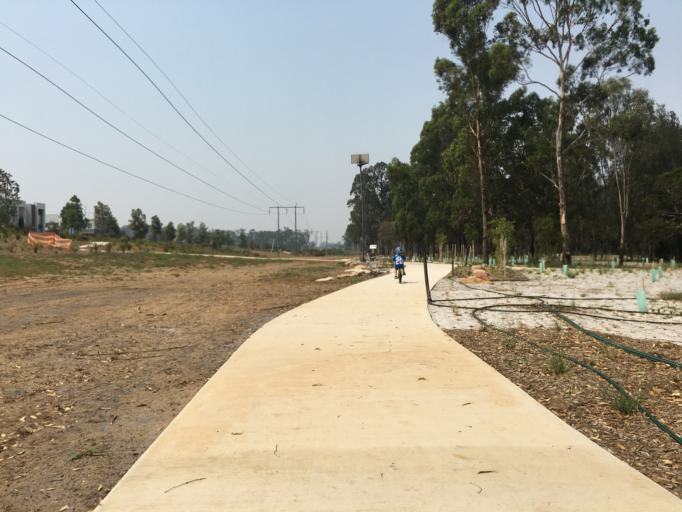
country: AU
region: New South Wales
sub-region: Campbelltown Municipality
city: Denham Court
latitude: -33.9760
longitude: 150.8145
